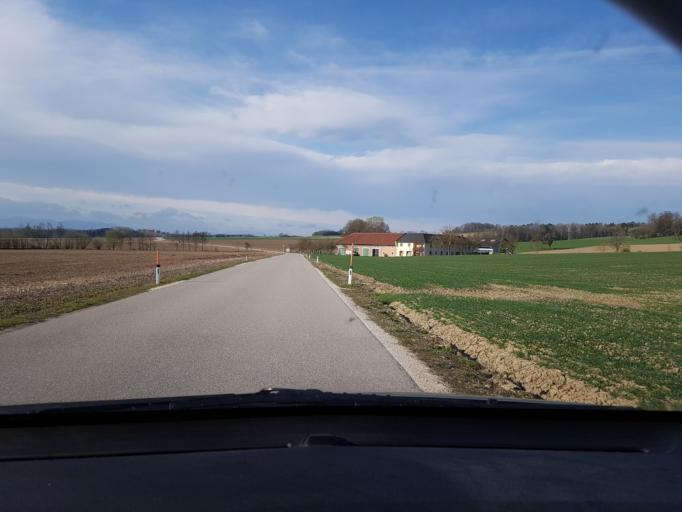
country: AT
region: Upper Austria
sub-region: Politischer Bezirk Linz-Land
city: Sankt Florian
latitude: 48.1725
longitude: 14.4090
